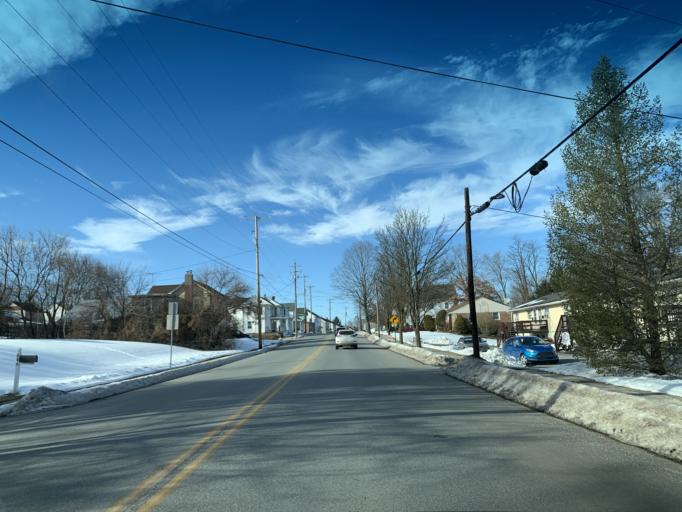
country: US
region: Pennsylvania
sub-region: York County
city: Dillsburg
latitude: 40.1038
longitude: -77.0331
